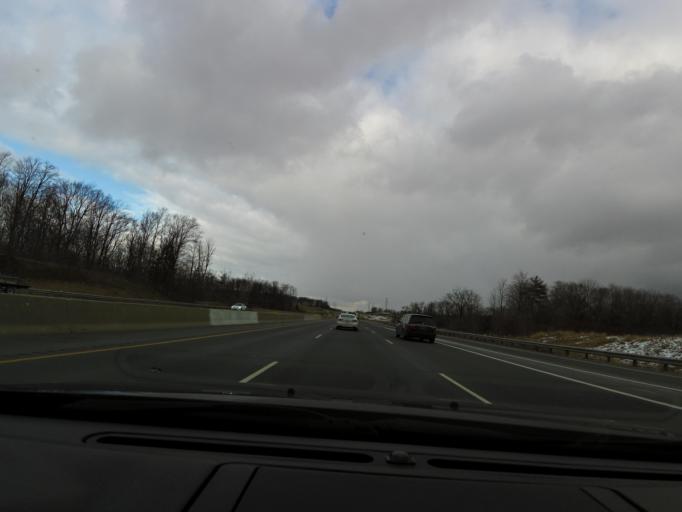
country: CA
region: Ontario
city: Burlington
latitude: 43.4180
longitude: -79.8173
